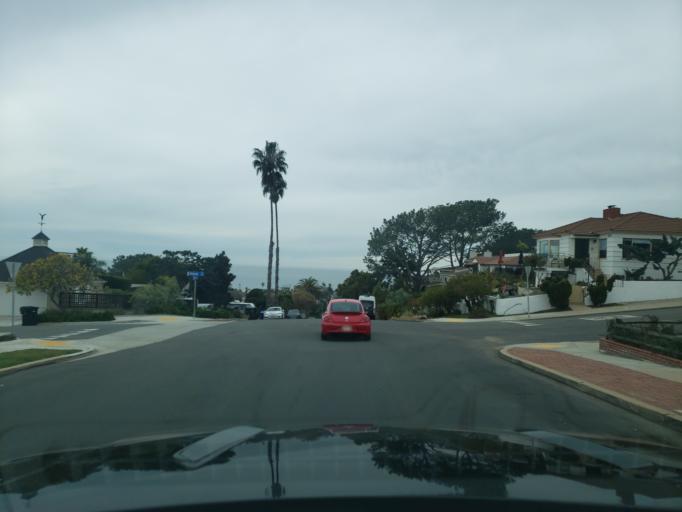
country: US
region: California
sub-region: San Diego County
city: Coronado
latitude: 32.7374
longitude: -117.2483
